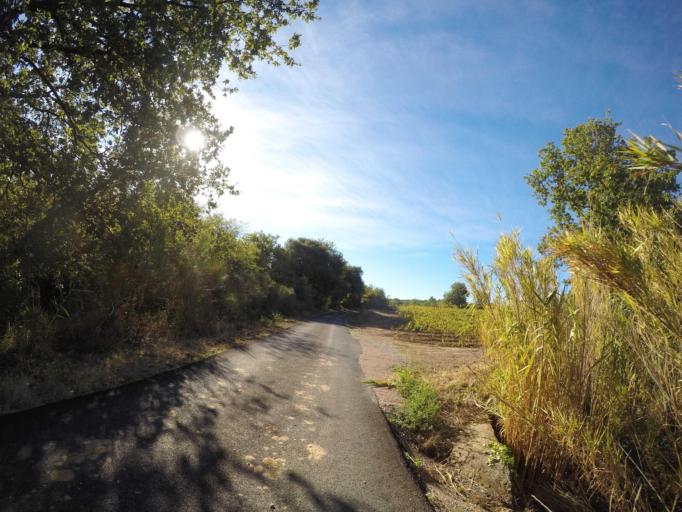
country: FR
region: Languedoc-Roussillon
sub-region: Departement des Pyrenees-Orientales
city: Trouillas
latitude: 42.5734
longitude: 2.7904
